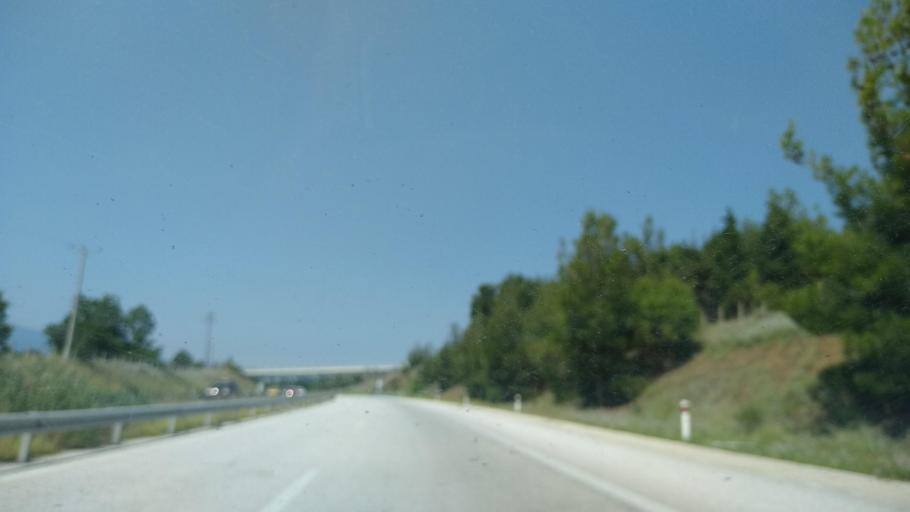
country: GR
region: Central Macedonia
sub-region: Nomos Thessalonikis
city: Askos
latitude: 40.6956
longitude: 23.3110
